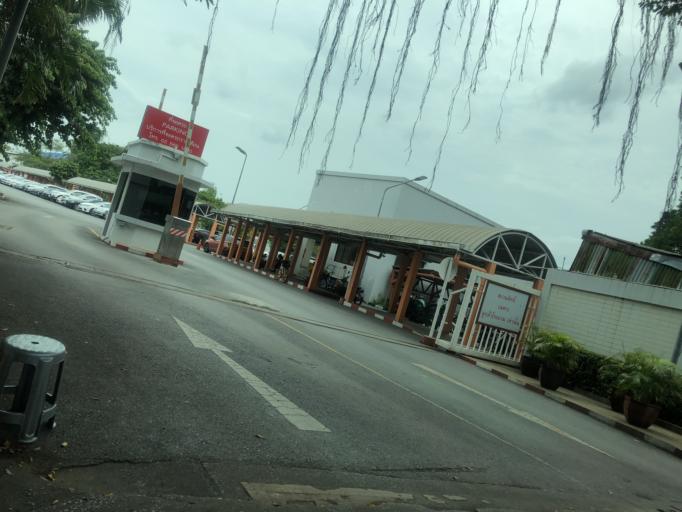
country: TH
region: Bangkok
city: Don Mueang
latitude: 13.9208
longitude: 100.5990
